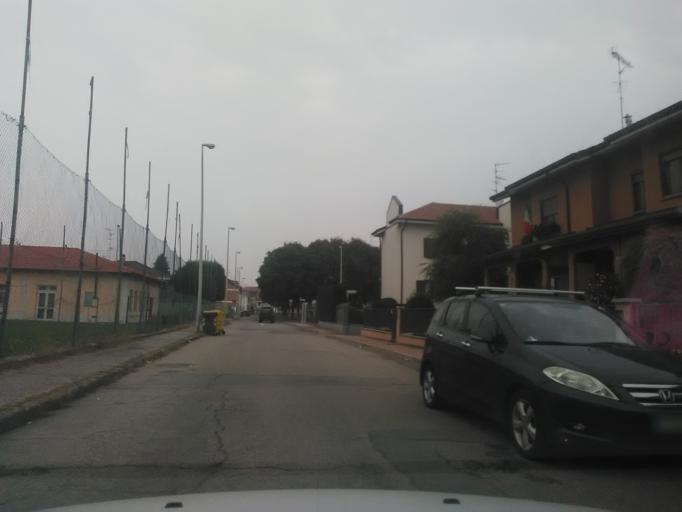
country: IT
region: Piedmont
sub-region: Provincia di Vercelli
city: Vercelli
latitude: 45.3243
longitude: 8.4055
